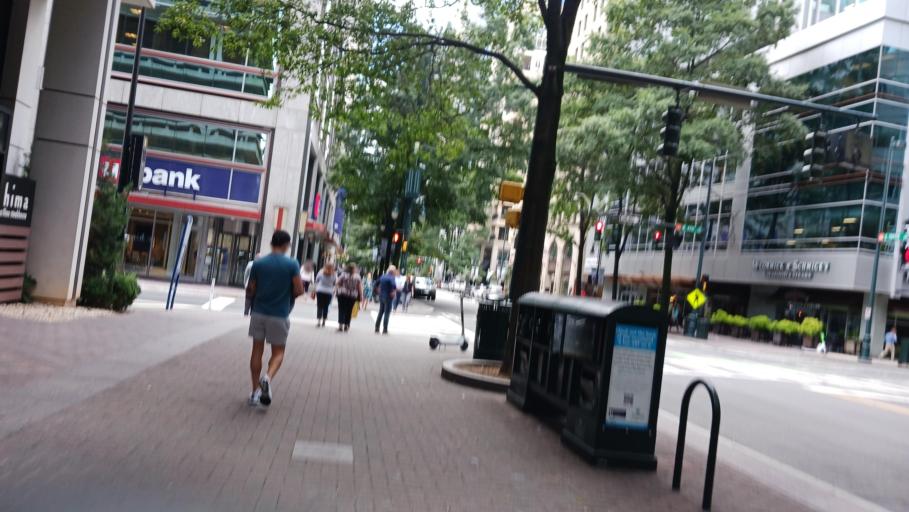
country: US
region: North Carolina
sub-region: Mecklenburg County
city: Charlotte
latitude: 35.2268
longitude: -80.8438
